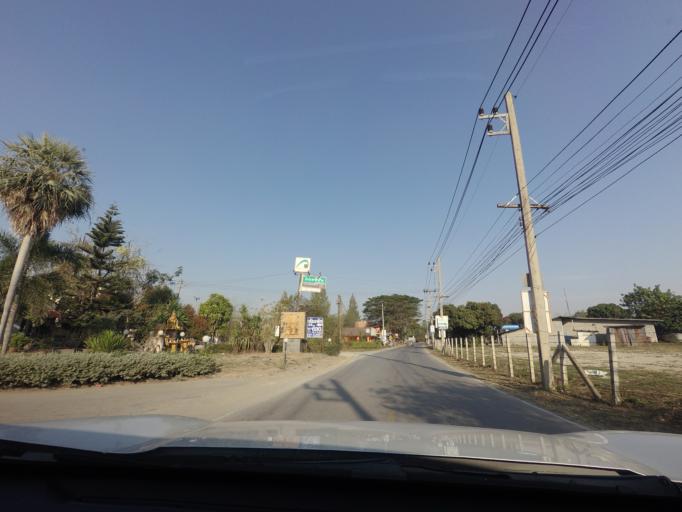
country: TH
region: Nakhon Ratchasima
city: Pak Chong
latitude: 14.6383
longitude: 101.4264
